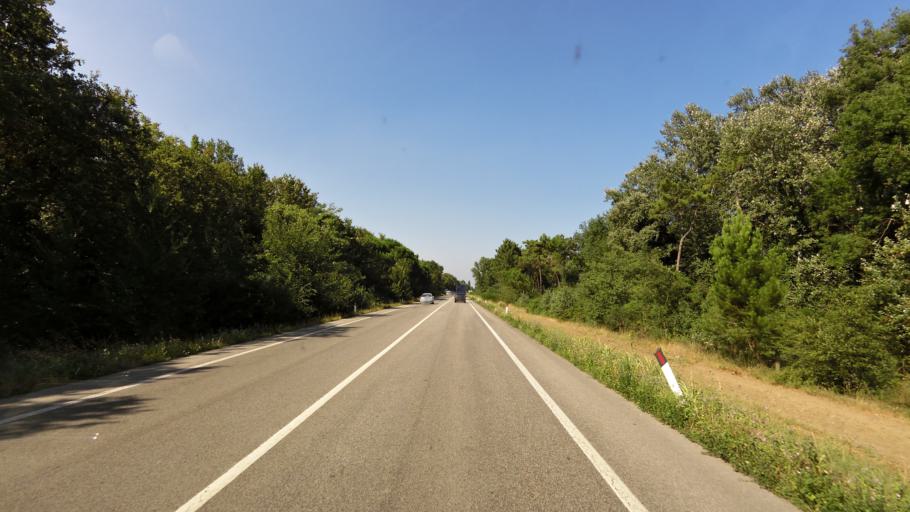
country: IT
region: Emilia-Romagna
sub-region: Provincia di Ravenna
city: Marina Romea
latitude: 44.4976
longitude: 12.2174
